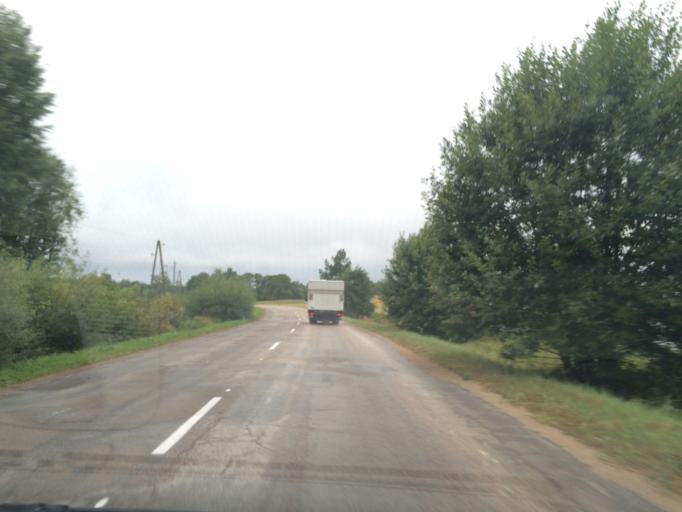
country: LV
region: Ikskile
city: Ikskile
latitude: 56.8556
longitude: 24.5288
